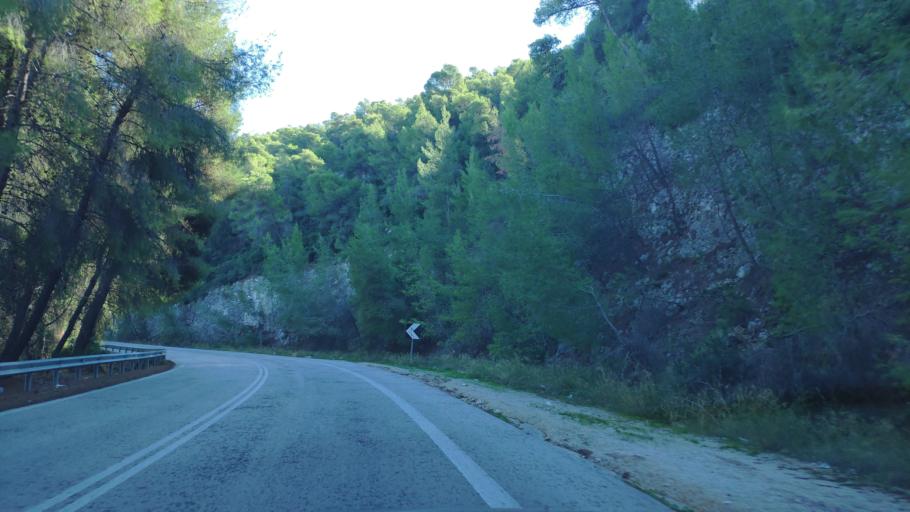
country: GR
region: Peloponnese
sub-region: Nomos Korinthias
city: Sofikon
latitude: 37.8277
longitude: 23.0722
